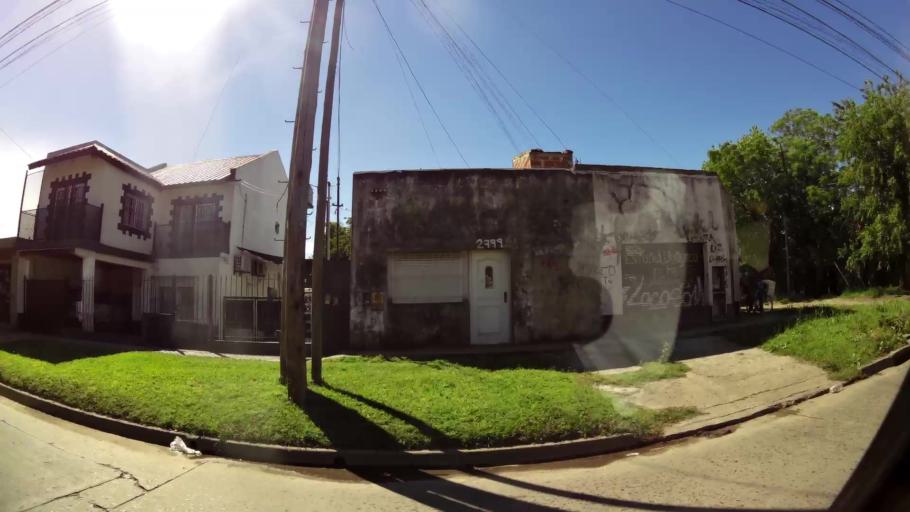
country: AR
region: Buenos Aires
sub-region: Partido de Almirante Brown
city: Adrogue
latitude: -34.8001
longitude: -58.3624
